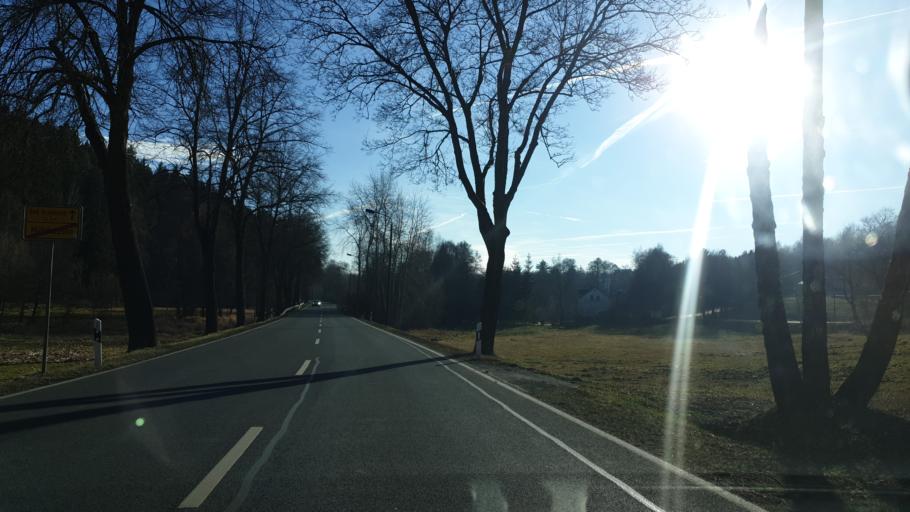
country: DE
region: Saxony
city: Adorf
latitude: 50.2863
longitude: 12.2740
